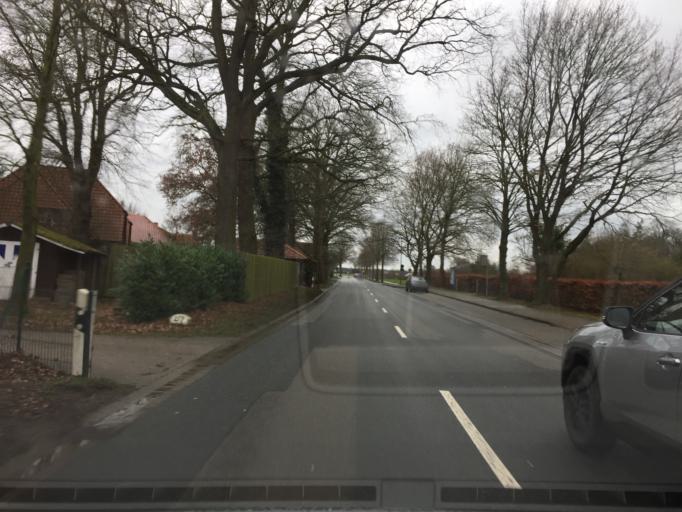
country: DE
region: Lower Saxony
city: Kirchseelte
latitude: 52.9790
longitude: 8.7088
